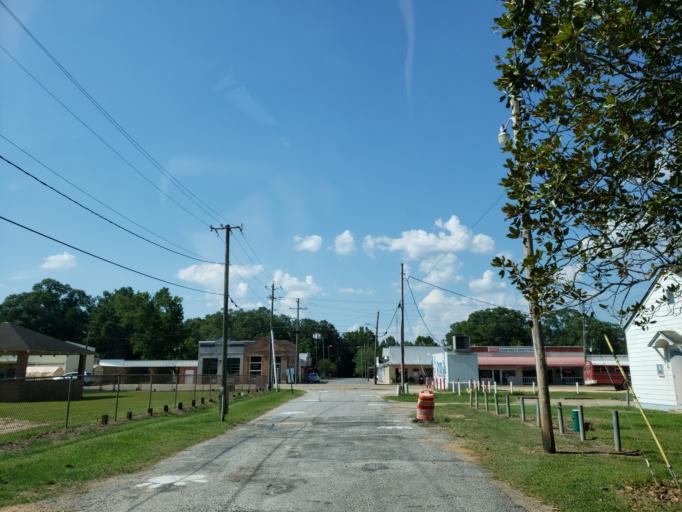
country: US
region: Mississippi
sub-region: Covington County
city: Collins
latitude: 31.5612
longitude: -89.4987
